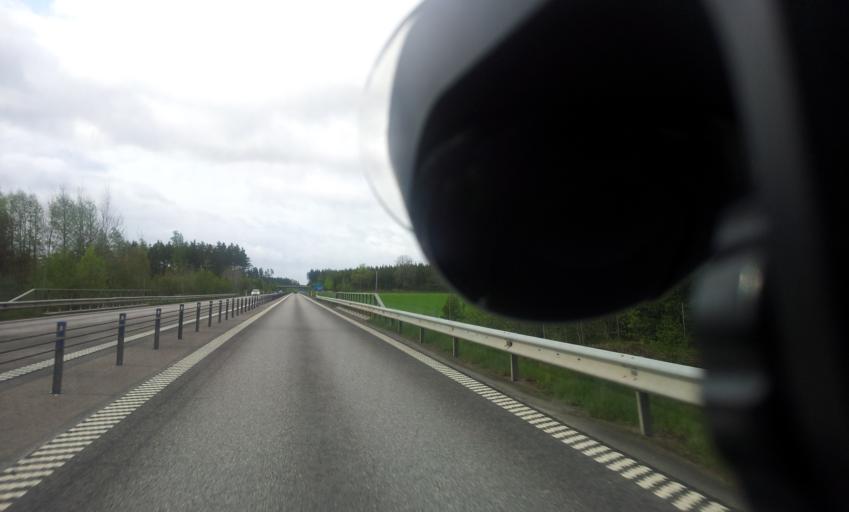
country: SE
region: Kalmar
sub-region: Torsas Kommun
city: Torsas
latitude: 56.5200
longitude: 16.0853
